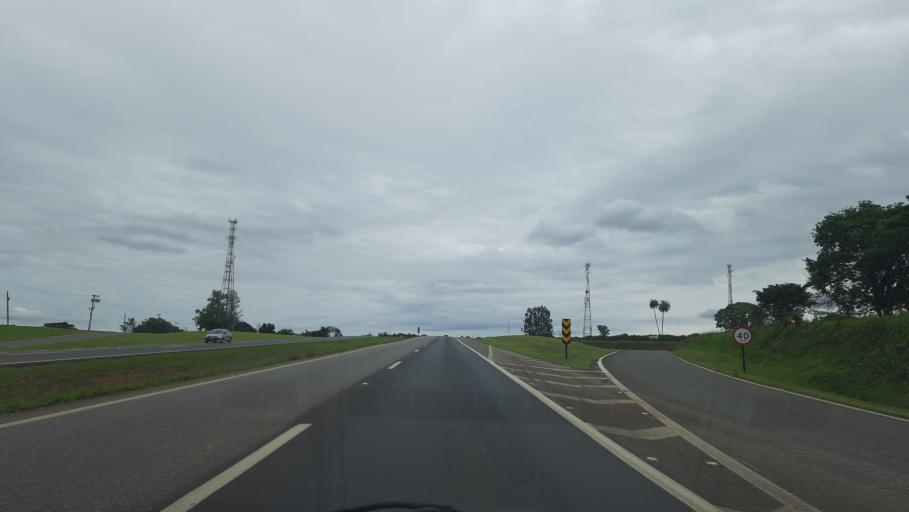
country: BR
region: Sao Paulo
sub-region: Moji-Guacu
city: Mogi-Gaucu
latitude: -22.2191
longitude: -46.9802
